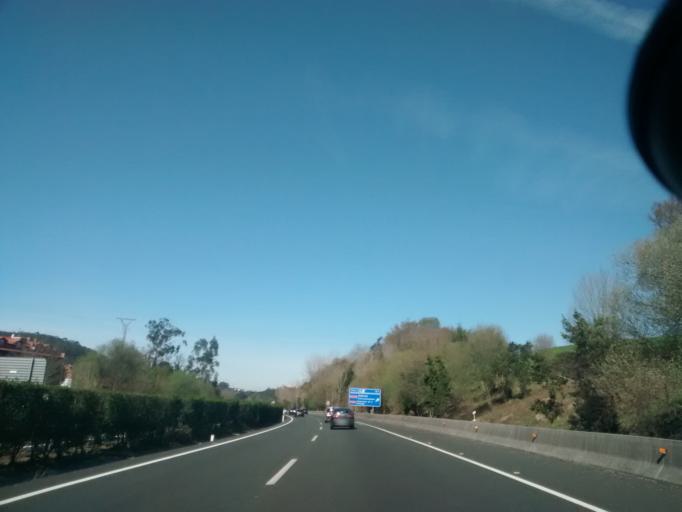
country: ES
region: Cantabria
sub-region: Provincia de Cantabria
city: Entrambasaguas
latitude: 43.3901
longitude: -3.6885
